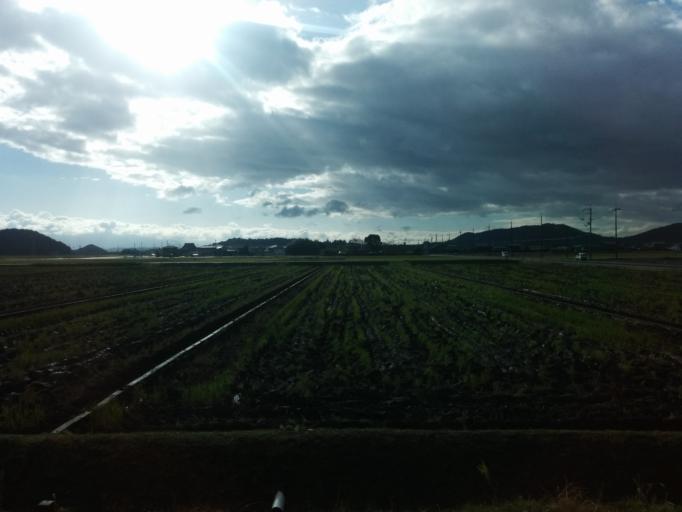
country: JP
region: Shiga Prefecture
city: Omihachiman
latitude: 35.1353
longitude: 136.1211
